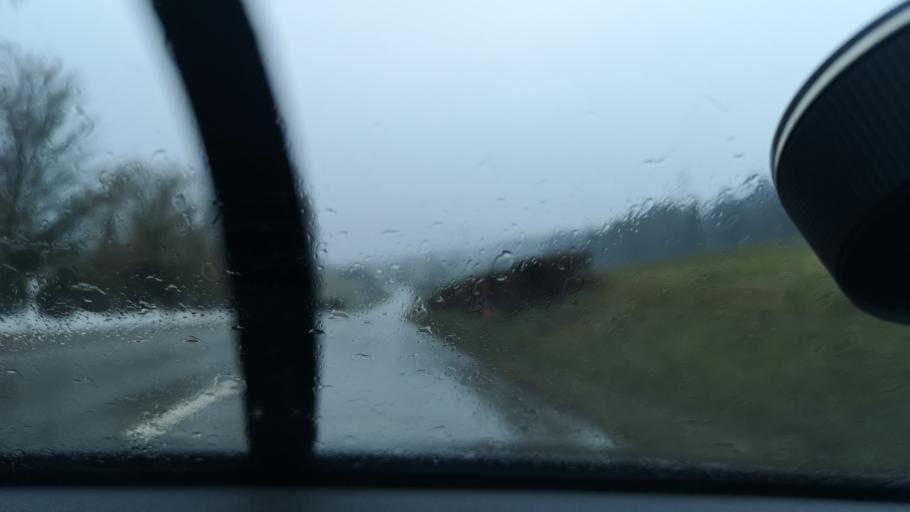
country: CH
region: Neuchatel
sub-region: Boudry District
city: Auvernier
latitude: 46.9860
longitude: 6.8612
